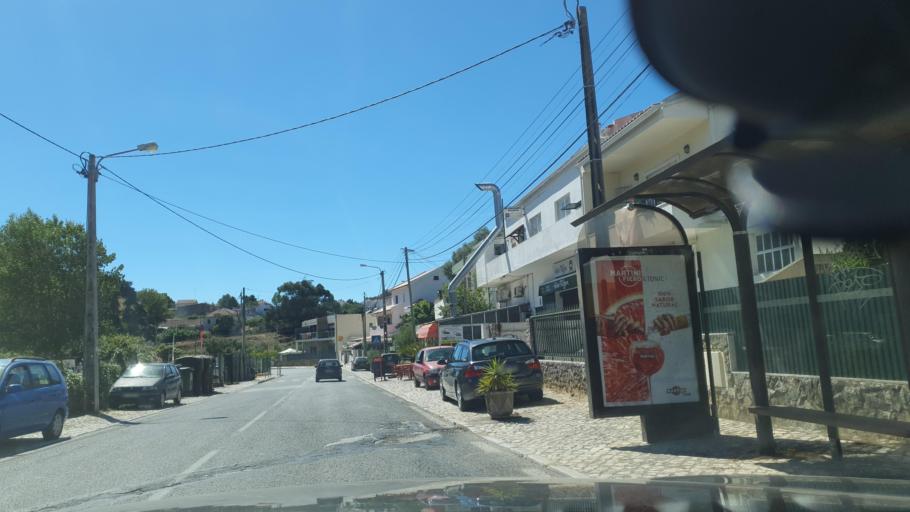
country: PT
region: Lisbon
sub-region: Sintra
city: Belas
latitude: 38.7815
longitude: -9.2500
